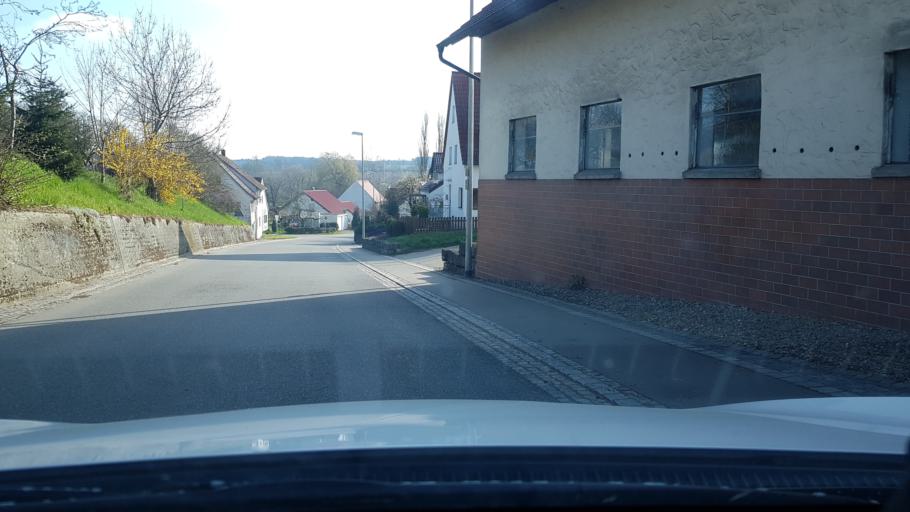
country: DE
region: Baden-Wuerttemberg
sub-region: Tuebingen Region
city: Schwendi
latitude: 48.1994
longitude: 9.9544
